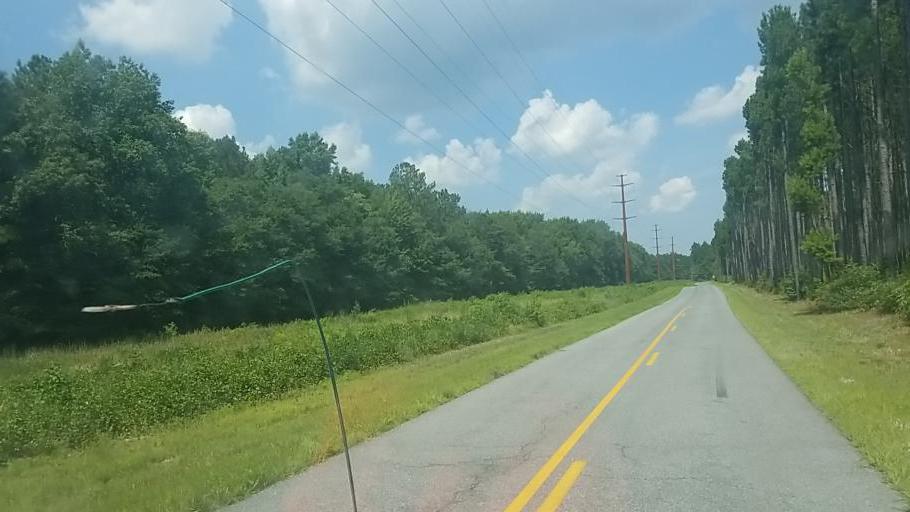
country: US
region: Maryland
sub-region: Worcester County
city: Snow Hill
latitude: 38.2649
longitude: -75.4671
